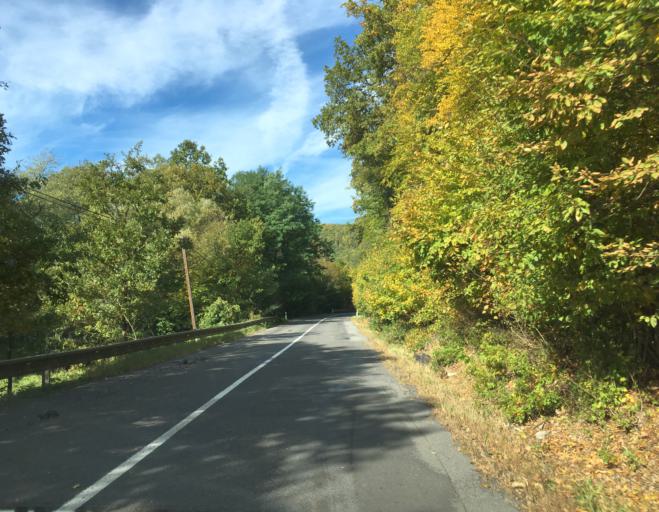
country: SK
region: Banskobystricky
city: Krupina
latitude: 48.3014
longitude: 18.9766
